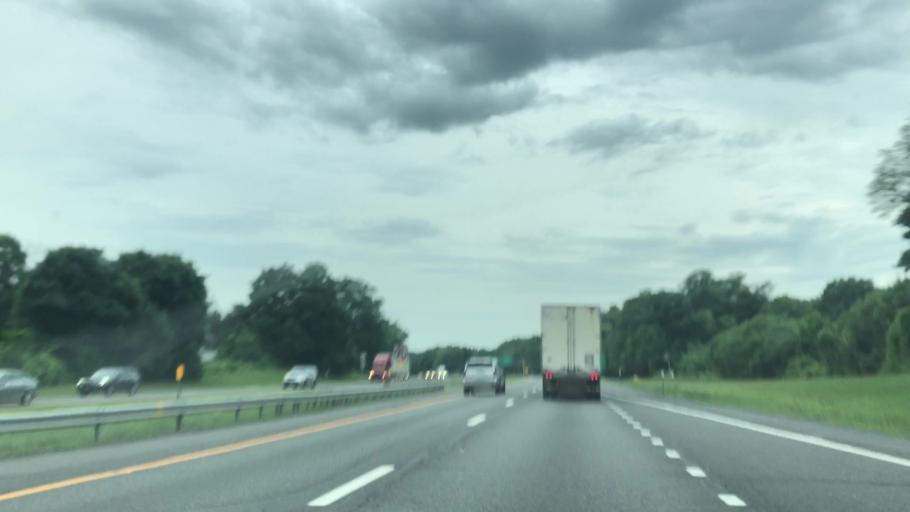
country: US
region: New York
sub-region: Rensselaer County
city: Castleton-on-Hudson
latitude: 42.5286
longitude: -73.7867
